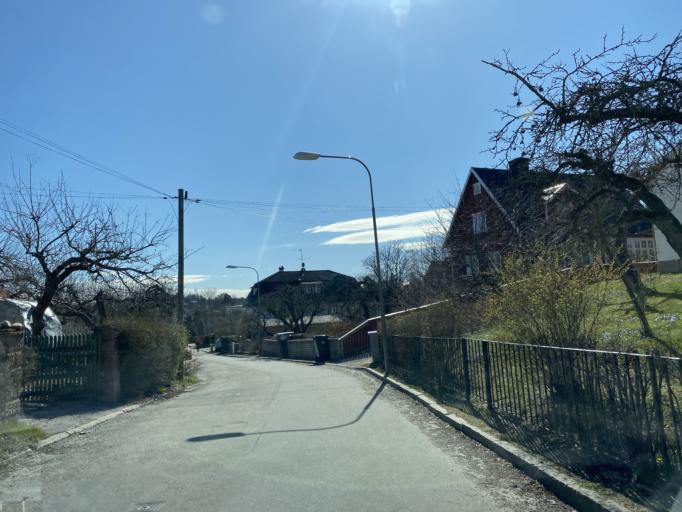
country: SE
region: Stockholm
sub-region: Stockholms Kommun
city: Arsta
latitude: 59.2813
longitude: 18.0554
